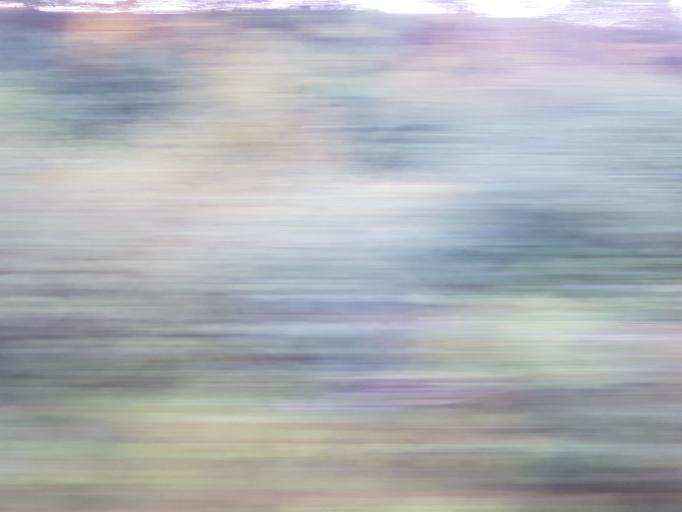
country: NO
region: Sor-Trondelag
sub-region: Melhus
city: Lundamo
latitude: 63.1464
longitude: 10.2756
